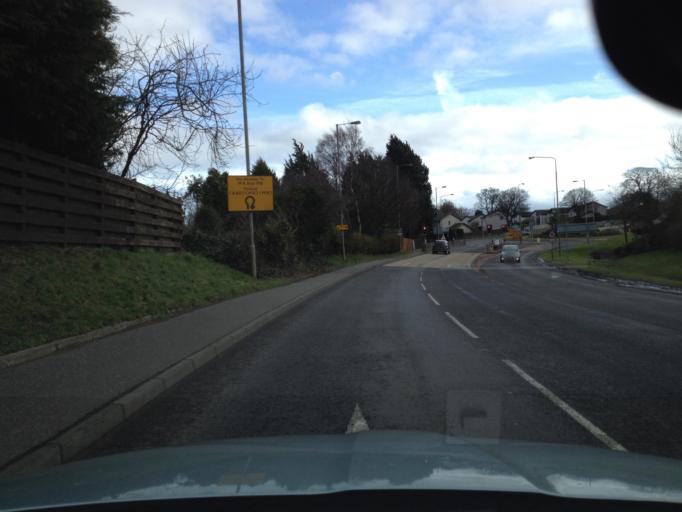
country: GB
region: Scotland
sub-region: Edinburgh
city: Queensferry
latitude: 55.9841
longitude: -3.3988
